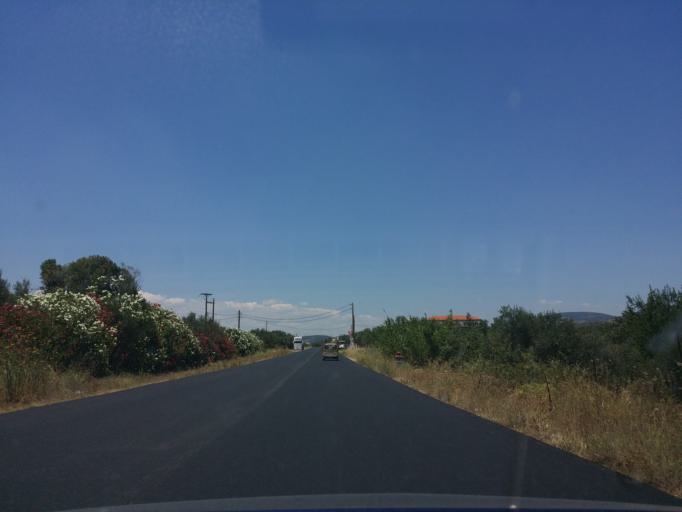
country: GR
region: Peloponnese
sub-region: Nomos Lakonias
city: Sparti
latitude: 37.0822
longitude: 22.4464
